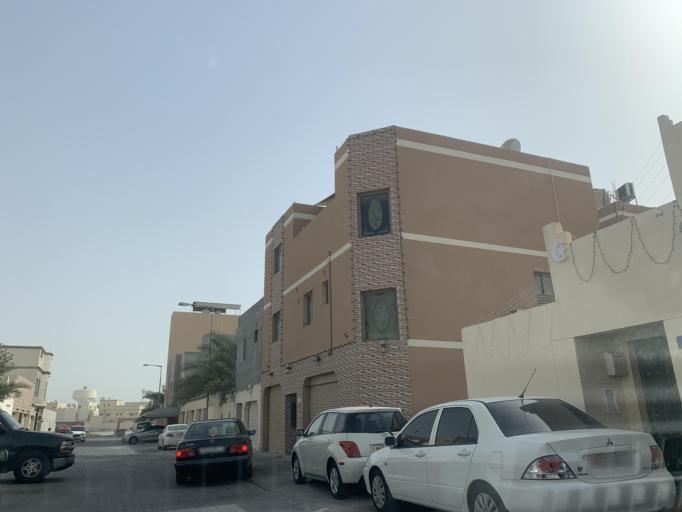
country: BH
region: Northern
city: Madinat `Isa
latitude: 26.1771
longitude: 50.5236
